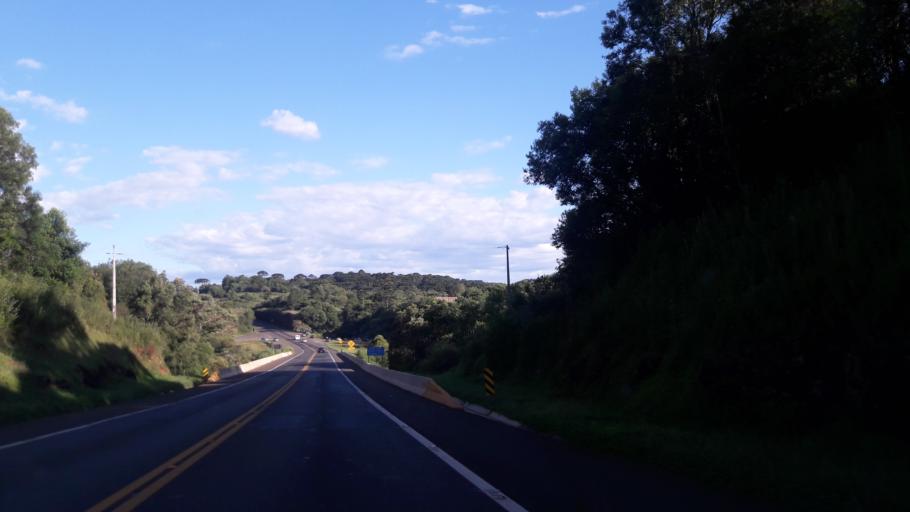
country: BR
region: Parana
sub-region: Guarapuava
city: Guarapuava
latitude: -25.3559
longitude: -51.3612
